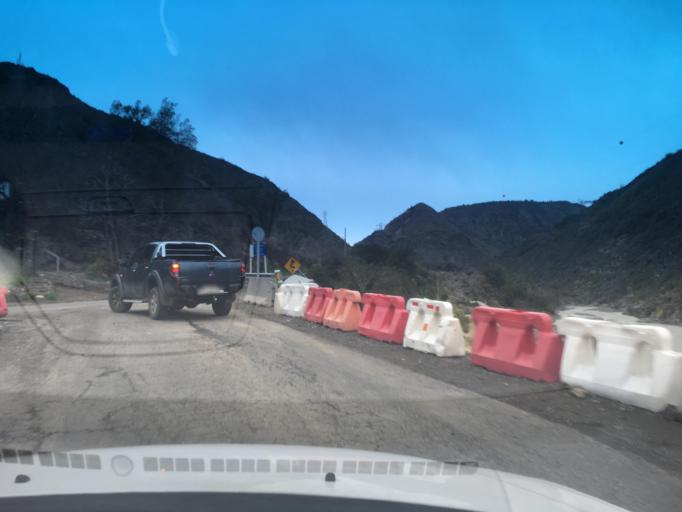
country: CL
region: Santiago Metropolitan
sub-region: Provincia de Cordillera
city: Puente Alto
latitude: -33.7344
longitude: -70.3010
